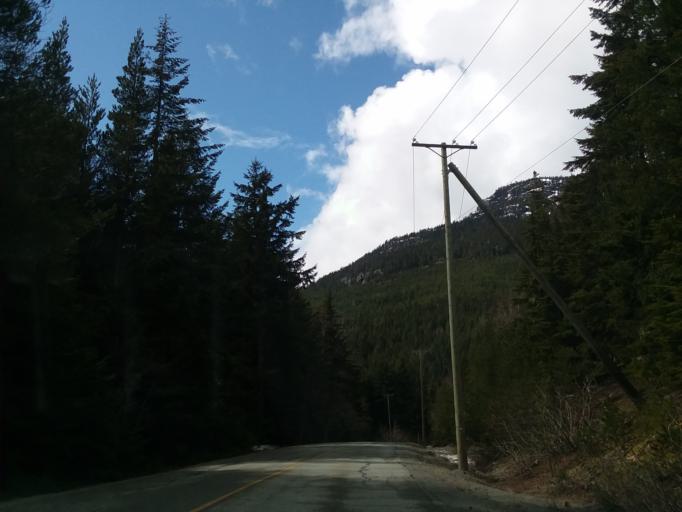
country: CA
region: British Columbia
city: Whistler
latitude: 50.1310
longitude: -122.9823
